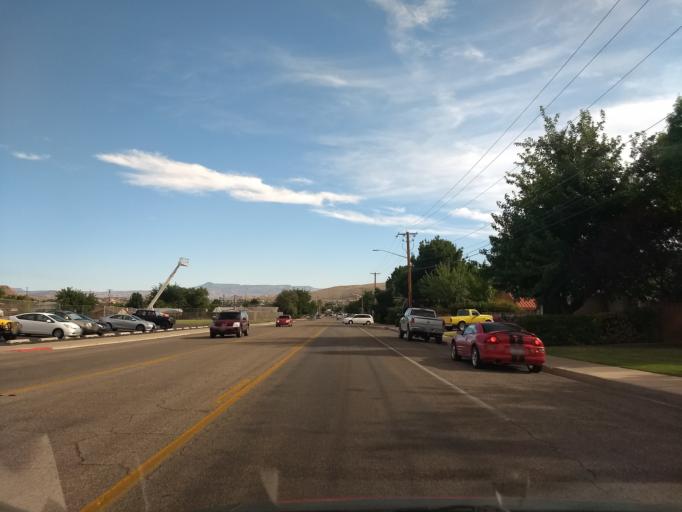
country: US
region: Utah
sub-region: Washington County
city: Saint George
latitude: 37.0995
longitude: -113.5686
